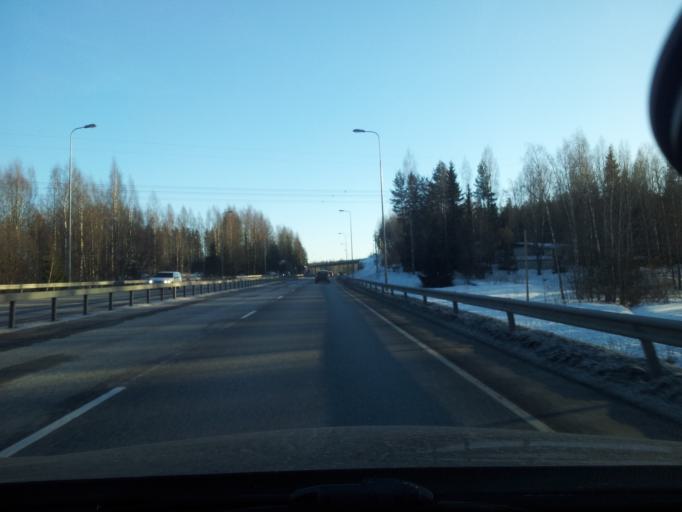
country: FI
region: Uusimaa
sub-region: Helsinki
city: Vihti
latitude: 60.3189
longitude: 24.3441
